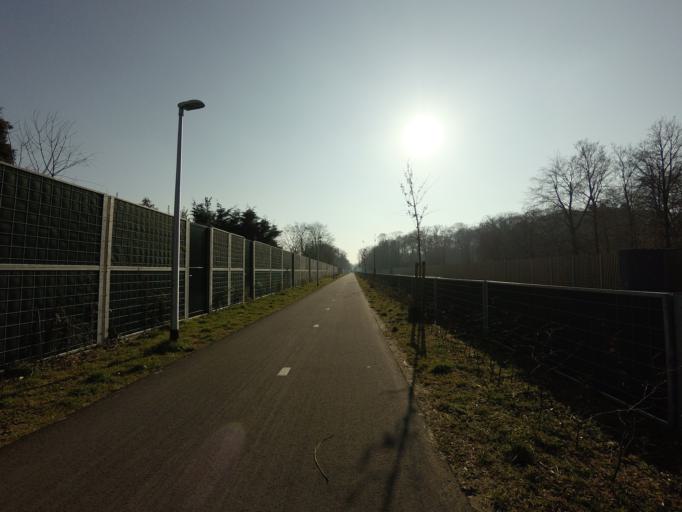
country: NL
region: North Holland
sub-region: Gemeente Velsen
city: Velsen-Zuid
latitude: 52.4485
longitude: 4.6328
